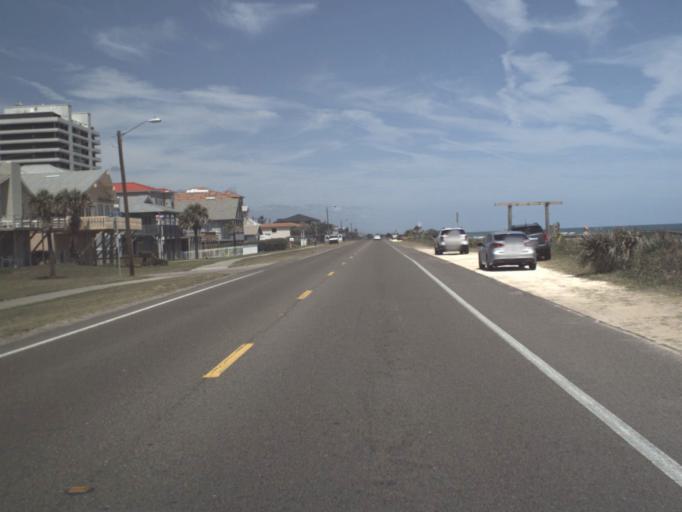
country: US
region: Florida
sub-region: Flagler County
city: Flagler Beach
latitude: 29.4939
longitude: -81.1337
